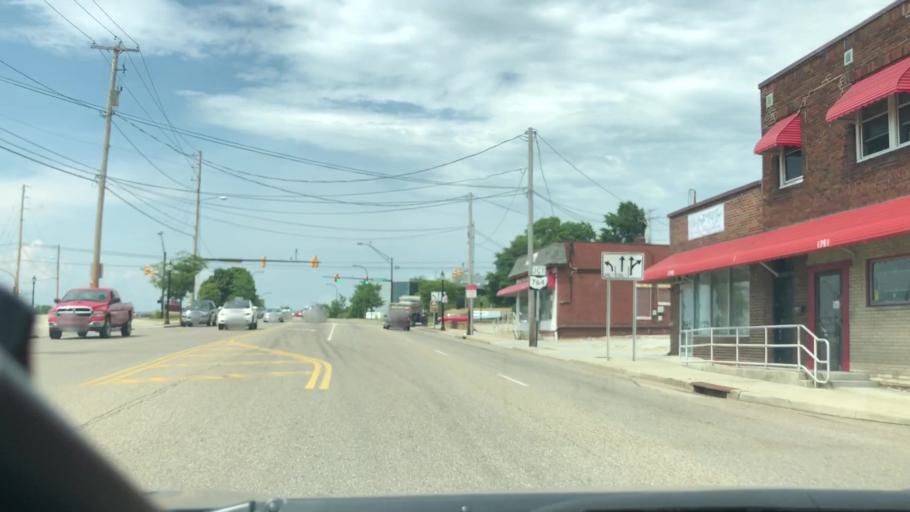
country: US
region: Ohio
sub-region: Summit County
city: Portage Lakes
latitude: 41.0391
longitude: -81.5268
